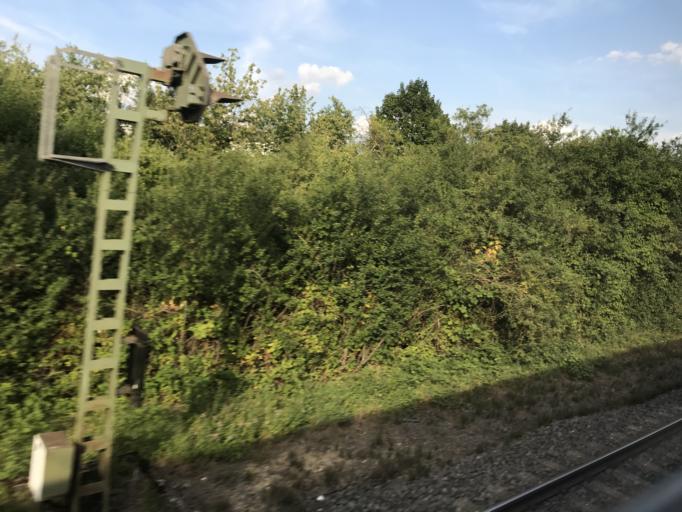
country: DE
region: Hesse
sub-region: Regierungsbezirk Giessen
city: Villmar
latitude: 50.3565
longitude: 8.1842
